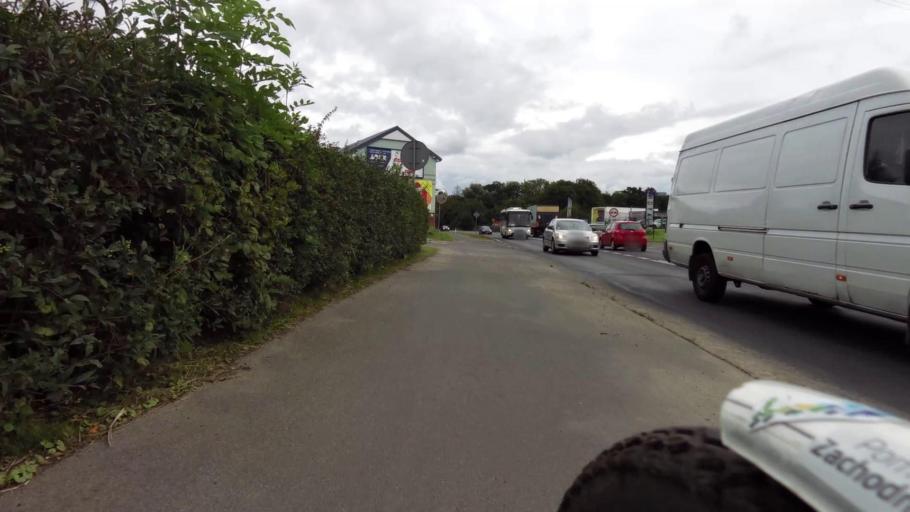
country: PL
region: West Pomeranian Voivodeship
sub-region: Powiat koszalinski
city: Mielno
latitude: 54.2178
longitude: 16.1073
